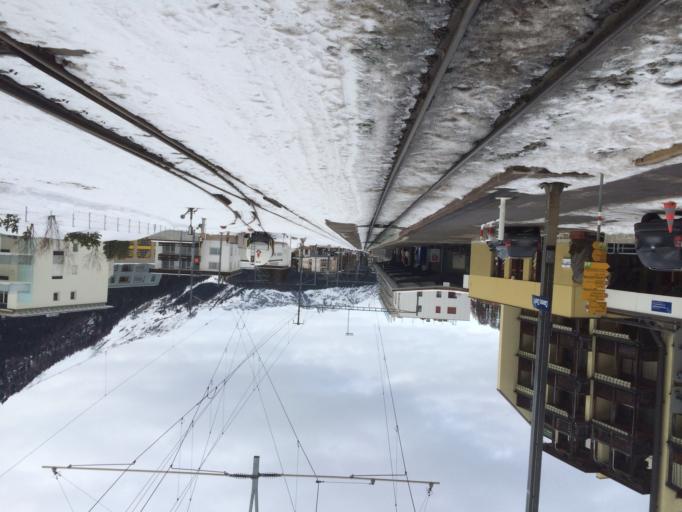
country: CH
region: Grisons
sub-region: Praettigau/Davos District
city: Davos
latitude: 46.8089
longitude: 9.8413
